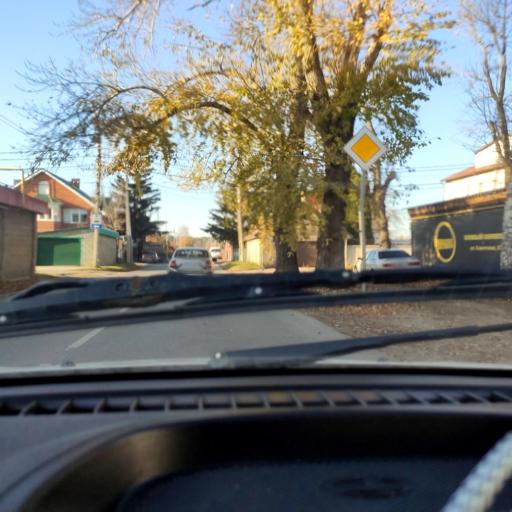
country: RU
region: Samara
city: Tol'yatti
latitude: 53.5133
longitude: 49.4011
